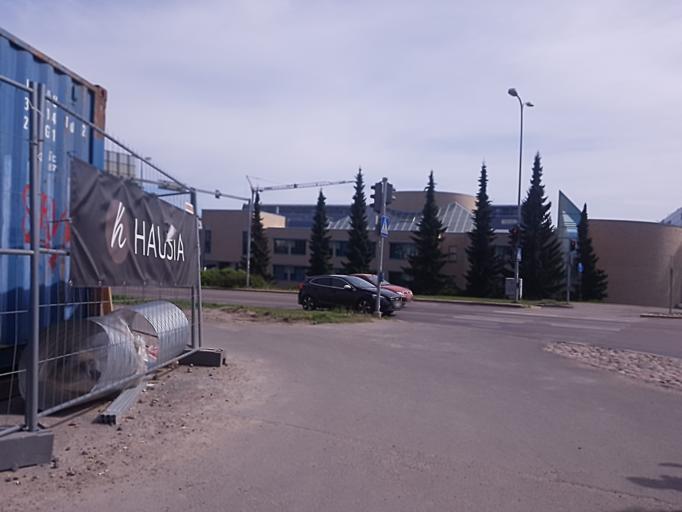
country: FI
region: Uusimaa
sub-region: Helsinki
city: Teekkarikylae
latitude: 60.2595
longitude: 24.8436
